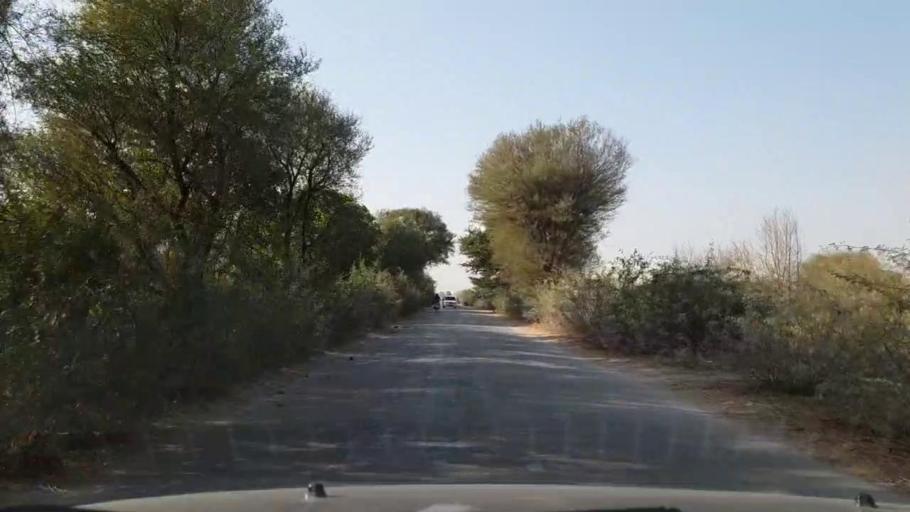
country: PK
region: Sindh
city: Tando Ghulam Ali
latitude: 25.1493
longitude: 68.8616
